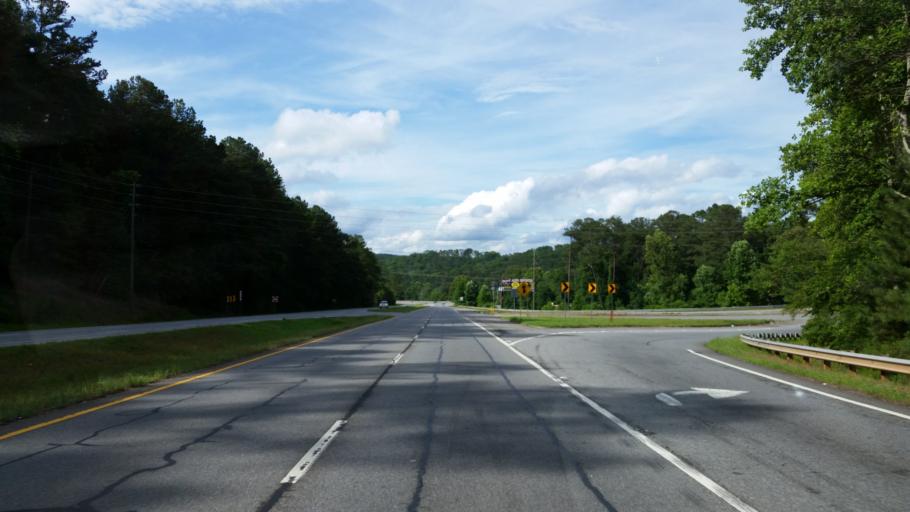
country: US
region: Georgia
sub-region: Bartow County
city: Emerson
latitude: 34.1410
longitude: -84.7487
